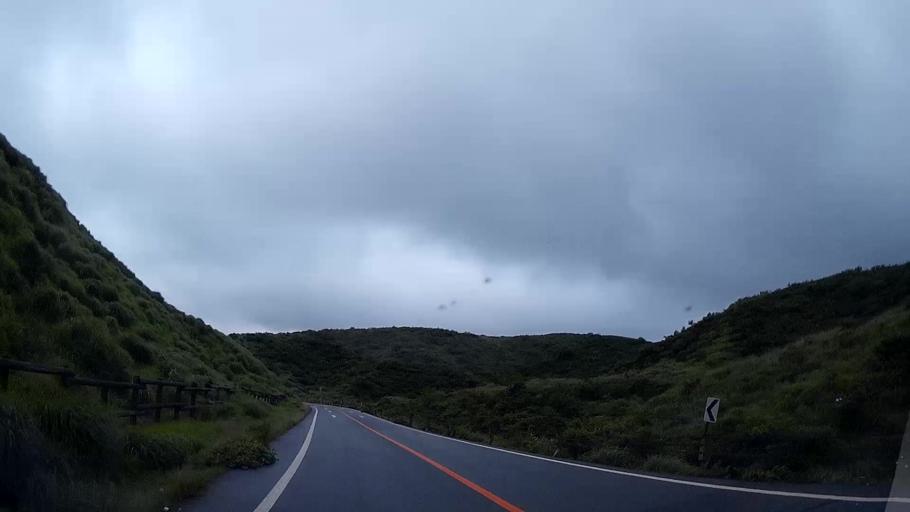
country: JP
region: Kumamoto
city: Aso
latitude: 32.8851
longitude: 131.0589
